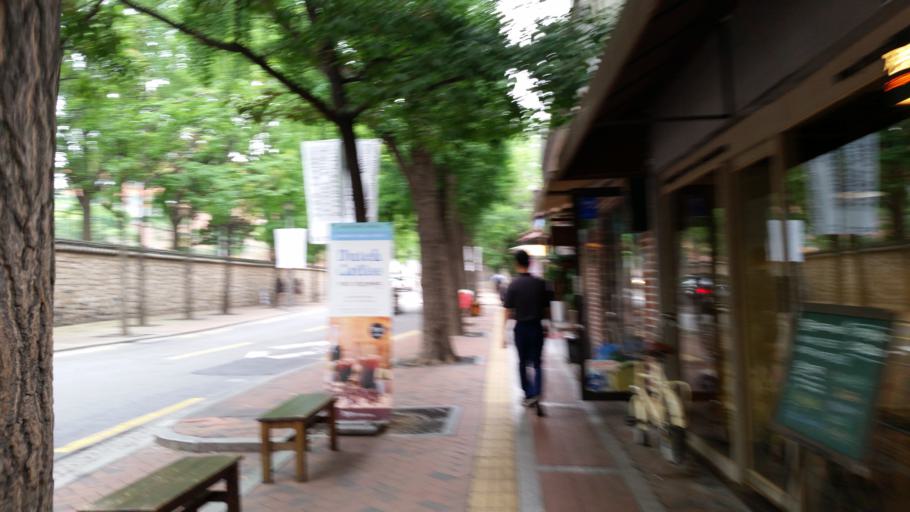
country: KR
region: Seoul
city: Seoul
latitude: 37.5659
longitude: 126.9725
